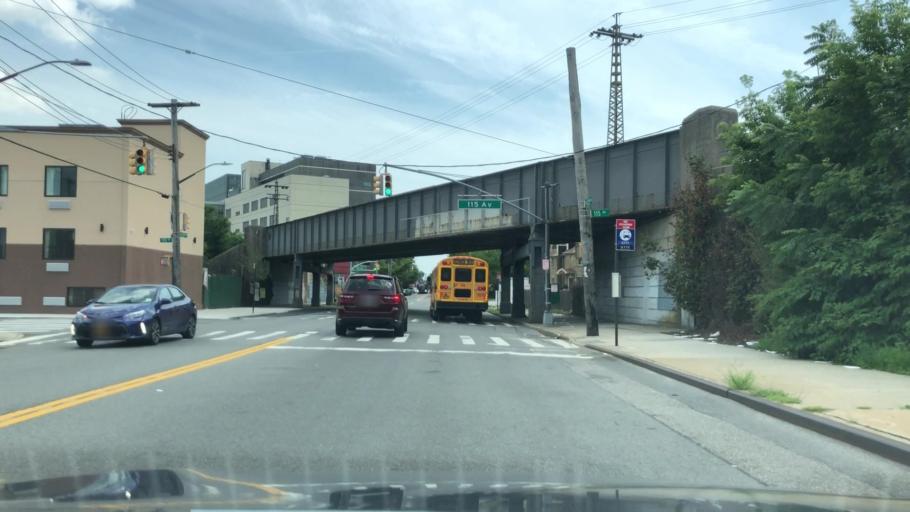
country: US
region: New York
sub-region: Queens County
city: Jamaica
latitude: 40.6878
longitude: -73.7851
